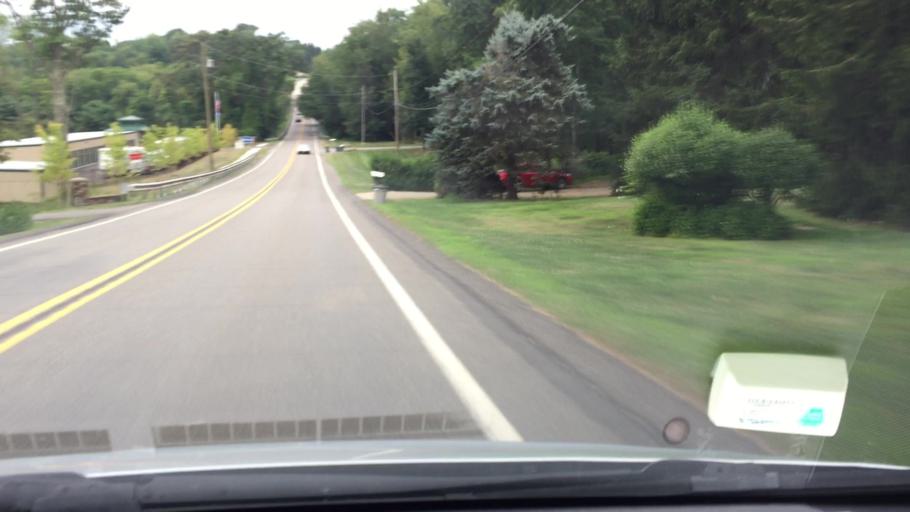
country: US
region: Pennsylvania
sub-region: Allegheny County
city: Franklin Park
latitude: 40.5875
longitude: -80.1025
